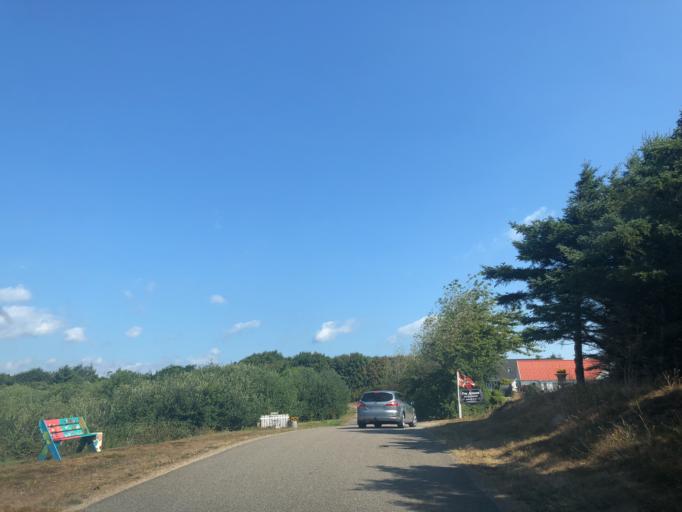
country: DK
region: North Denmark
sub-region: Morso Kommune
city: Nykobing Mors
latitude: 56.8043
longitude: 8.9979
